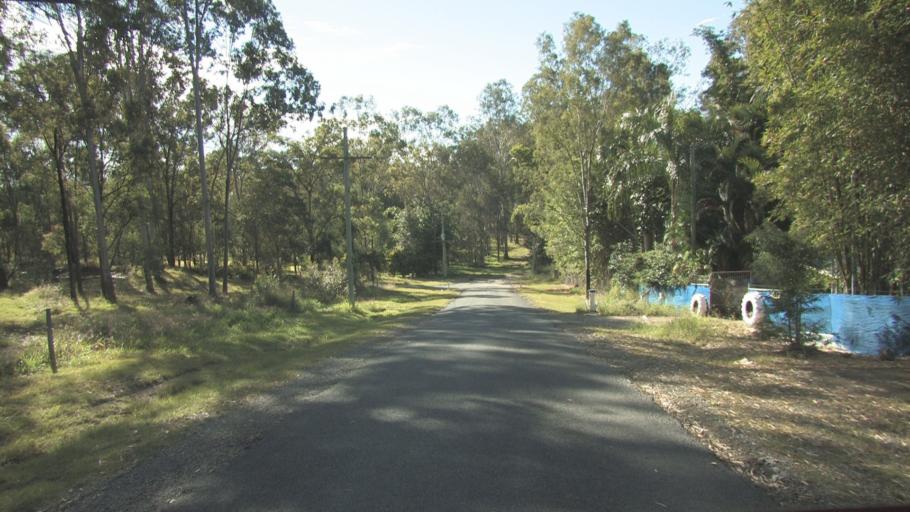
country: AU
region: Queensland
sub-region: Logan
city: Chambers Flat
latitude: -27.8217
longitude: 153.0799
